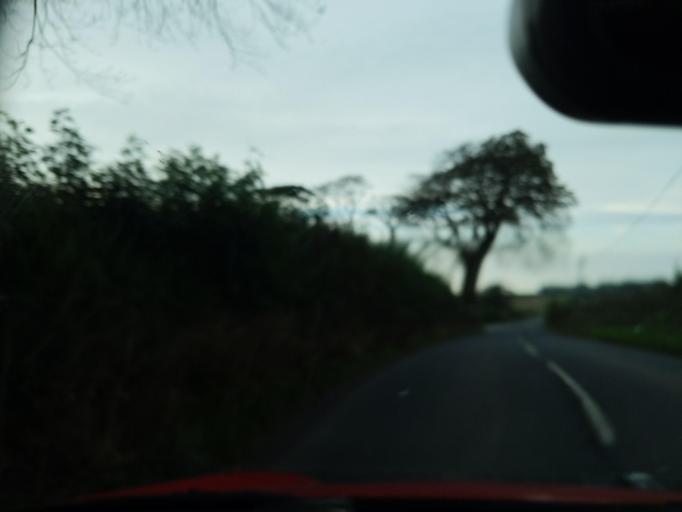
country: GB
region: England
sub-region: Devon
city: Great Torrington
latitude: 50.9252
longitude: -4.1479
